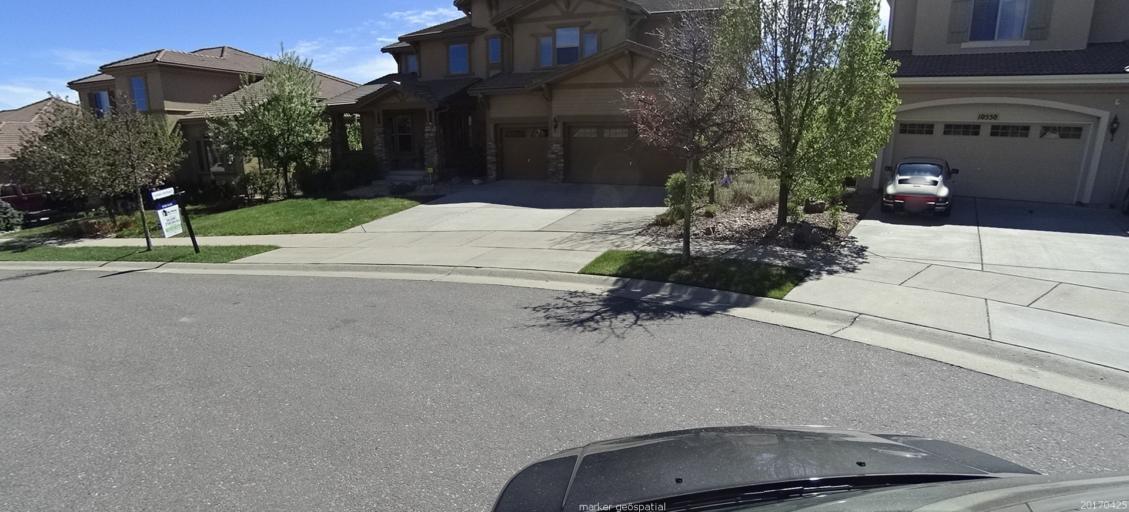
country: US
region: Colorado
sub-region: Douglas County
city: Carriage Club
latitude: 39.5247
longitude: -104.8838
